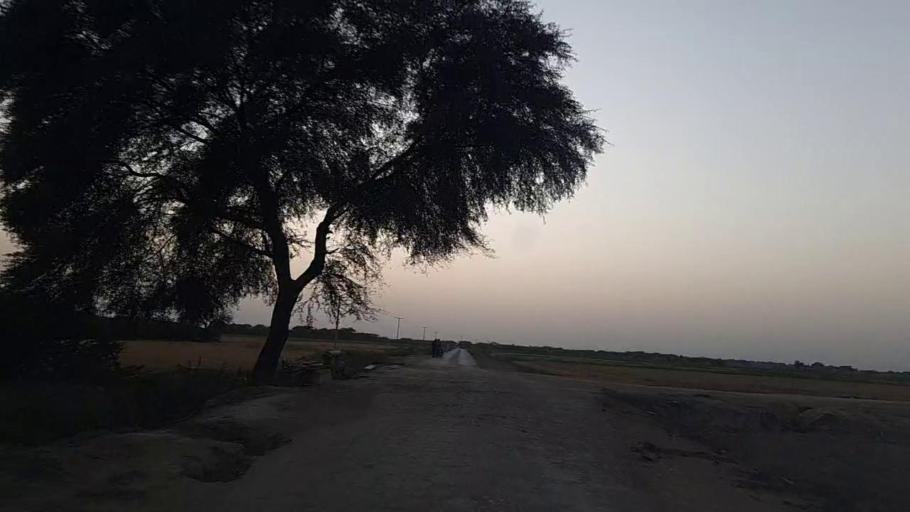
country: PK
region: Sindh
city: Naukot
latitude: 24.7532
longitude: 69.2877
